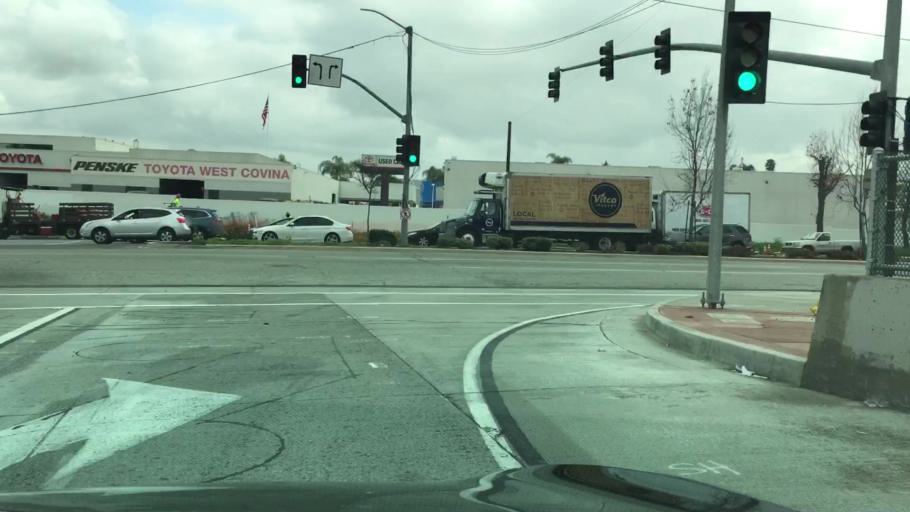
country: US
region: California
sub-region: Los Angeles County
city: Covina
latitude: 34.0712
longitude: -117.9080
